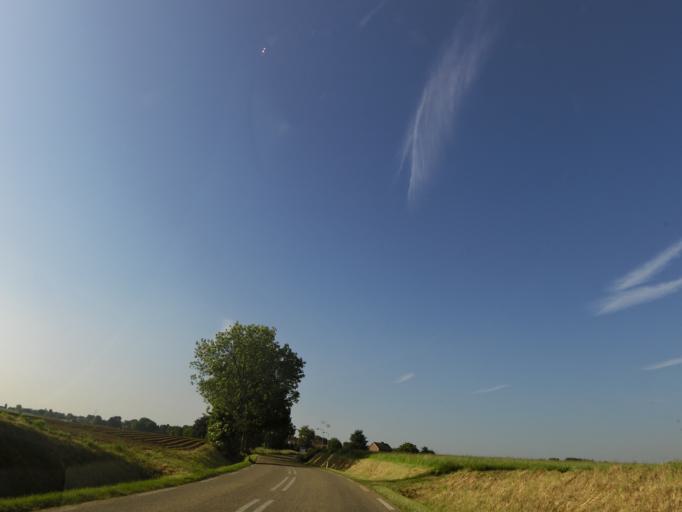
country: NL
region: Limburg
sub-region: Gemeente Beek
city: Beek
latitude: 50.9151
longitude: 5.8106
